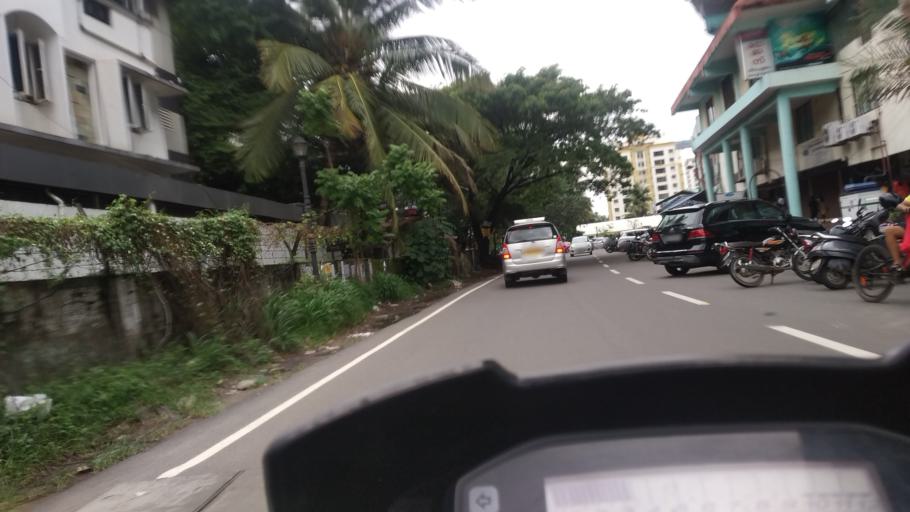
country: IN
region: Kerala
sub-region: Ernakulam
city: Elur
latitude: 9.9979
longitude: 76.3018
